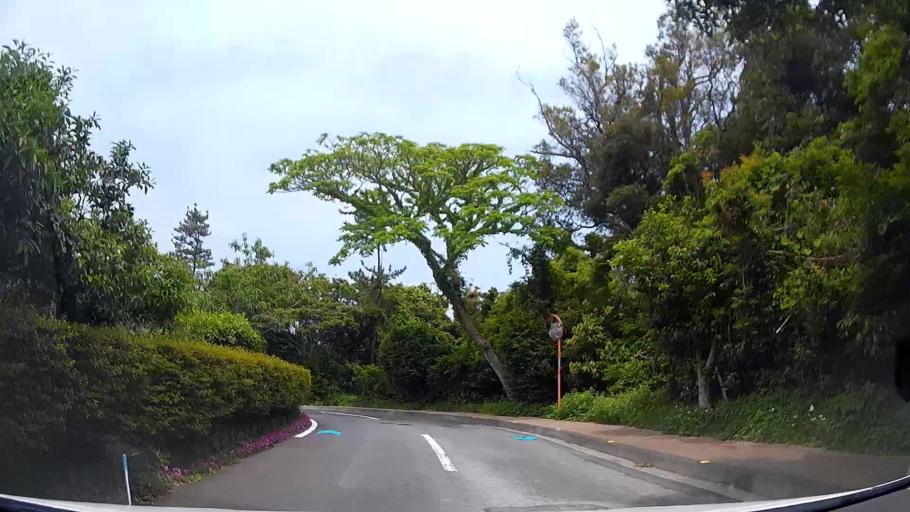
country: JP
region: Shizuoka
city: Ito
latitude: 34.8921
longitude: 139.1383
